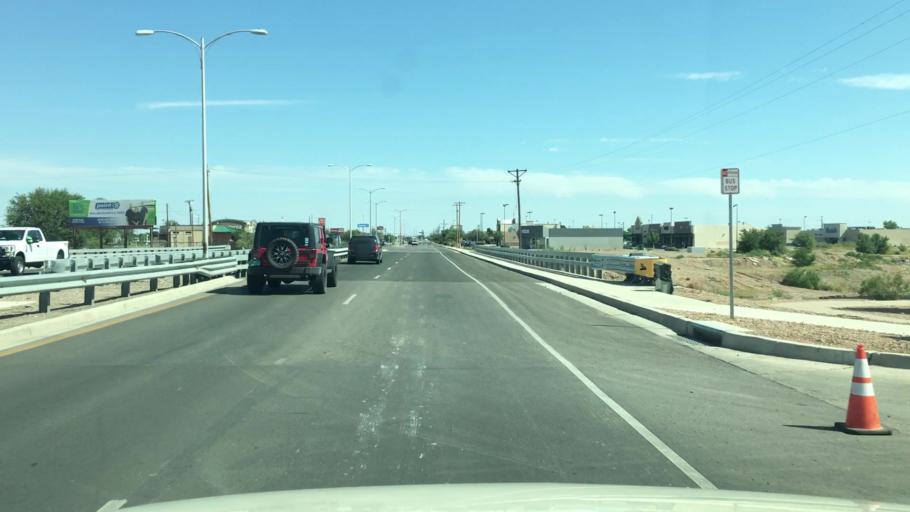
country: US
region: New Mexico
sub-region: Chaves County
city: Roswell
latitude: 33.4443
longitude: -104.5232
